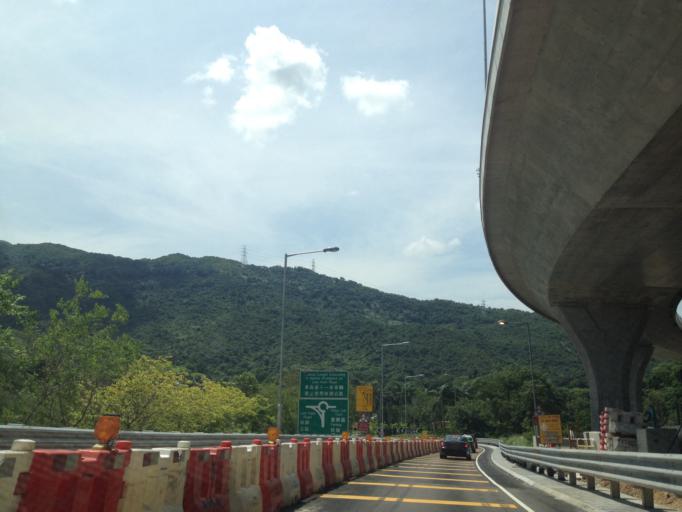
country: HK
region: Tai Po
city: Tai Po
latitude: 22.4589
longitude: 114.1475
